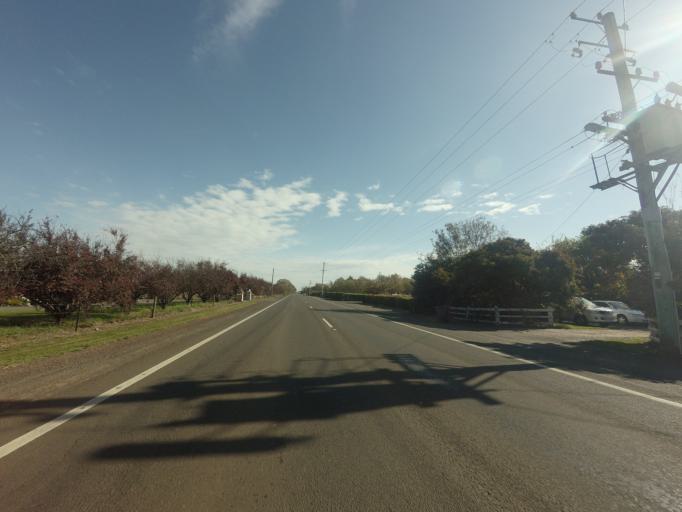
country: AU
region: Tasmania
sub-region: Meander Valley
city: Westbury
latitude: -41.5261
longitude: 146.8891
